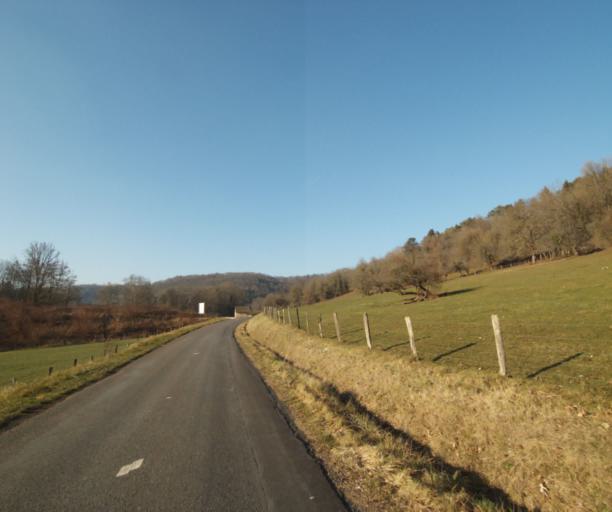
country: FR
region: Champagne-Ardenne
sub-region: Departement de la Haute-Marne
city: Chevillon
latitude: 48.5022
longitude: 5.1789
